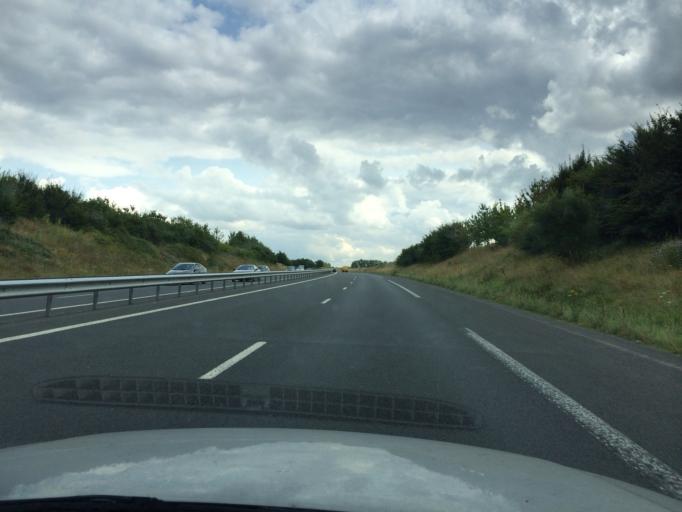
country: FR
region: Lower Normandy
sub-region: Departement du Calvados
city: Port-en-Bessin-Huppain
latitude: 49.3059
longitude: -0.8201
